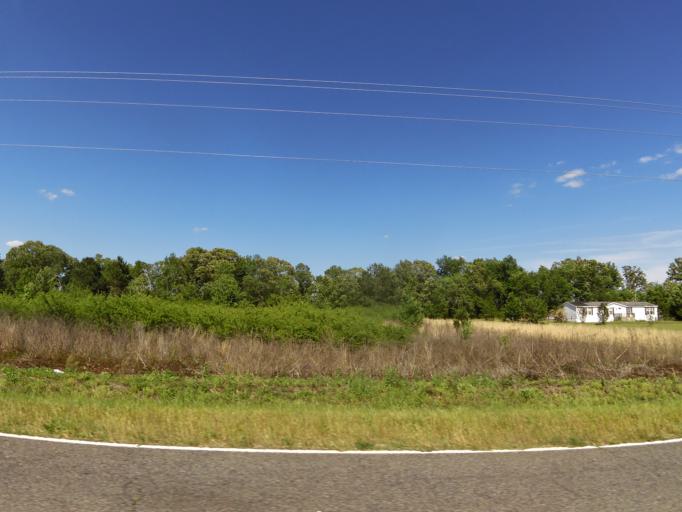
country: US
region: South Carolina
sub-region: Barnwell County
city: Williston
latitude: 33.4583
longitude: -81.4970
